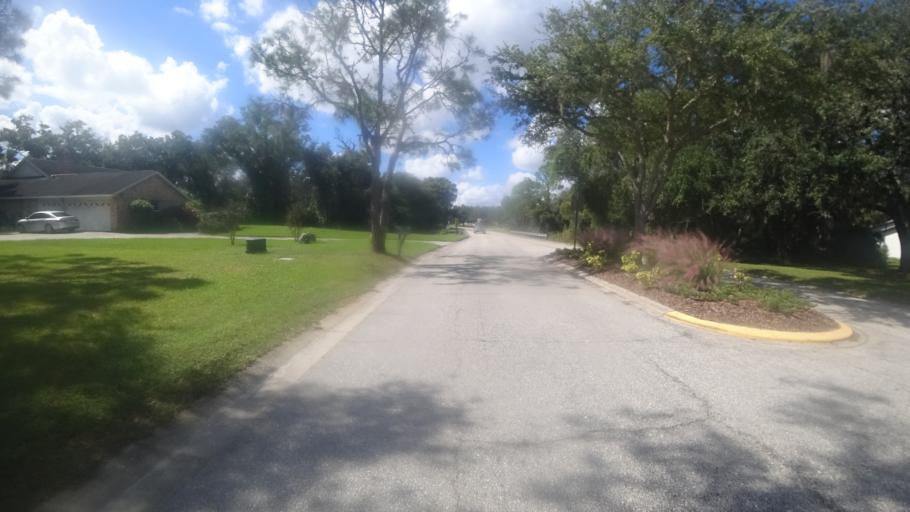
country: US
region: Florida
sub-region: Manatee County
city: Ellenton
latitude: 27.4859
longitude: -82.4062
